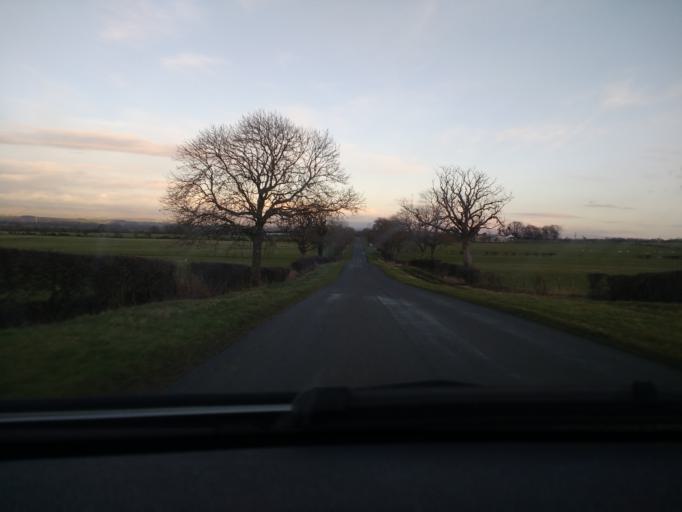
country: GB
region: England
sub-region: Cumbria
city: Carlisle
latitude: 54.7316
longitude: -2.9524
